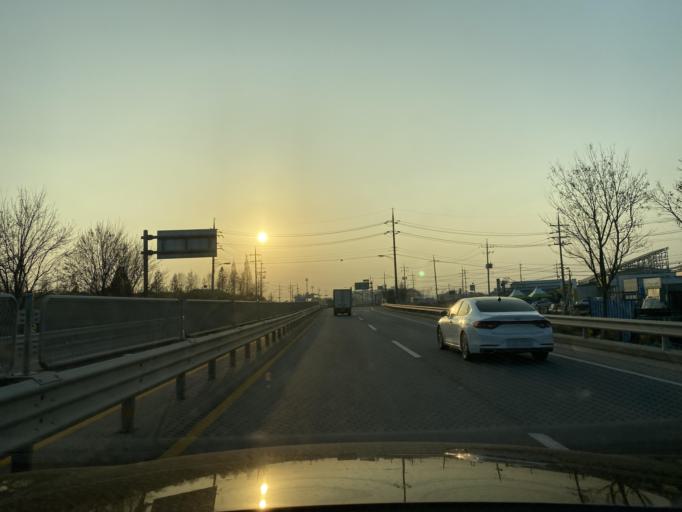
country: KR
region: Chungcheongnam-do
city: Yesan
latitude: 36.6882
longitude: 126.7860
